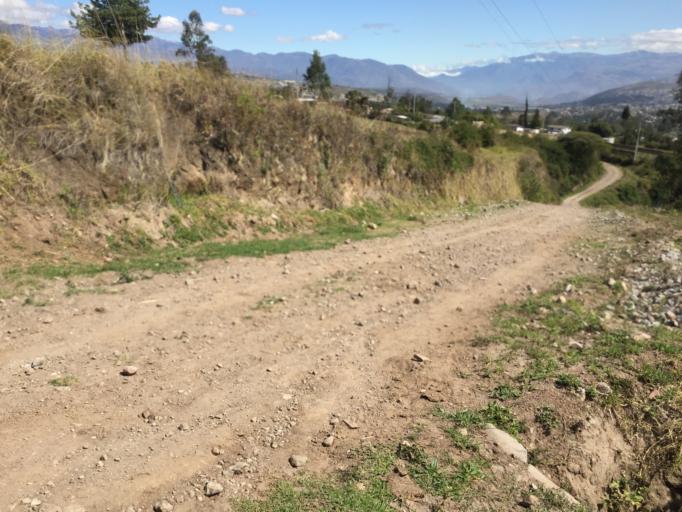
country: EC
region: Imbabura
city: Ibarra
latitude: 0.3100
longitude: -78.1578
